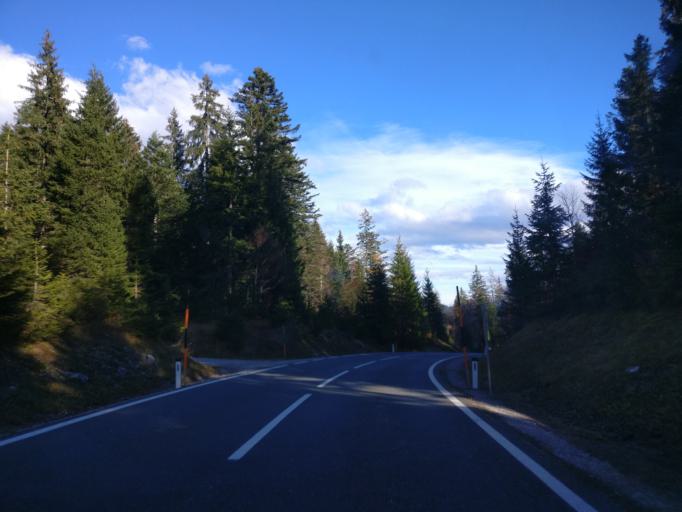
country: AT
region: Salzburg
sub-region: Politischer Bezirk Sankt Johann im Pongau
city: Muhlbach am Hochkonig
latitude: 47.3937
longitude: 13.0714
